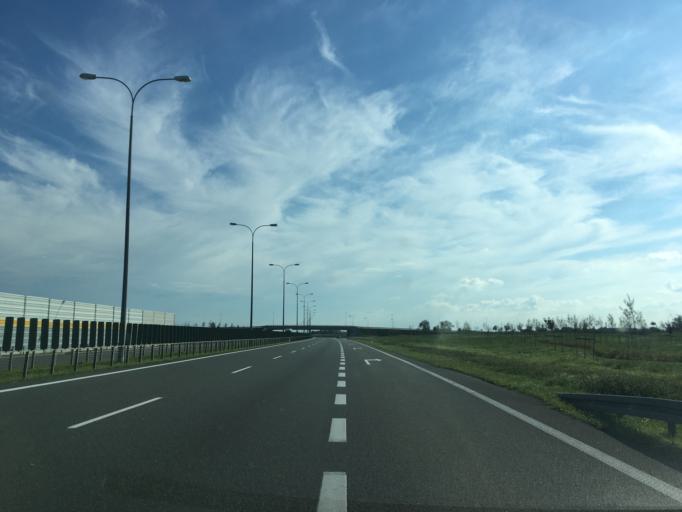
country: PL
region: Kujawsko-Pomorskie
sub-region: Powiat chelminski
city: Lisewo
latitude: 53.2921
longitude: 18.7075
